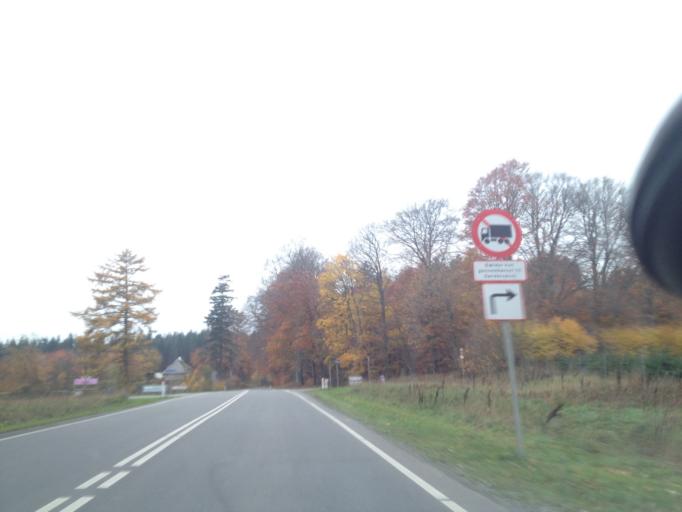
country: DK
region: South Denmark
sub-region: Nordfyns Kommune
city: Sonderso
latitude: 55.4390
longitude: 10.2162
